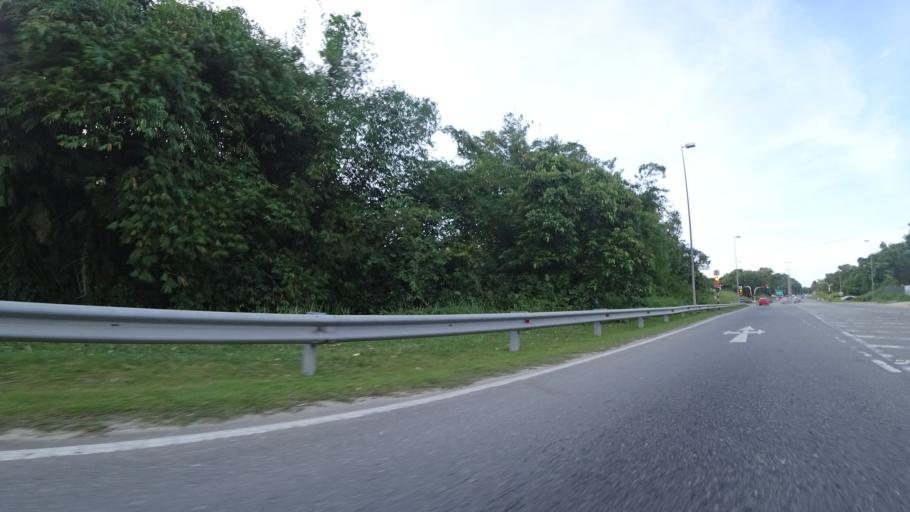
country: BN
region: Brunei and Muara
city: Bandar Seri Begawan
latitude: 4.8900
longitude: 114.9105
